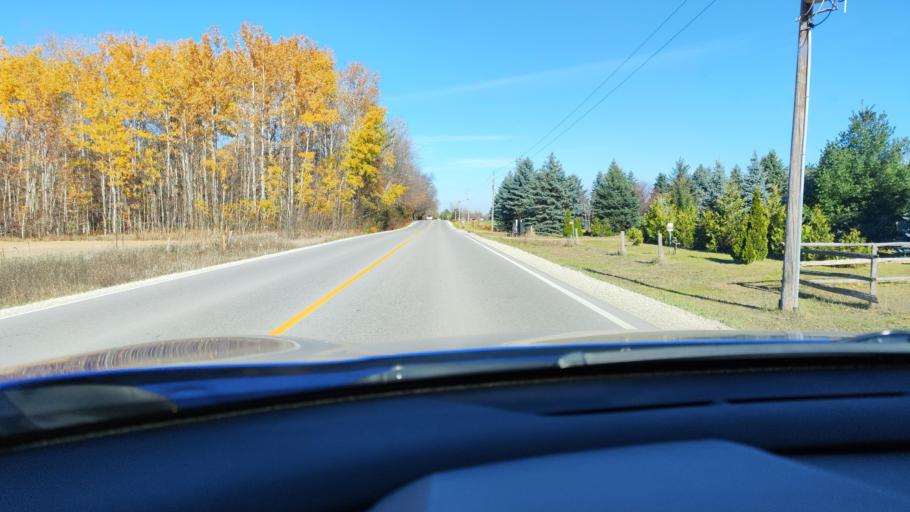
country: CA
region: Ontario
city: Wasaga Beach
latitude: 44.4101
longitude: -80.0601
